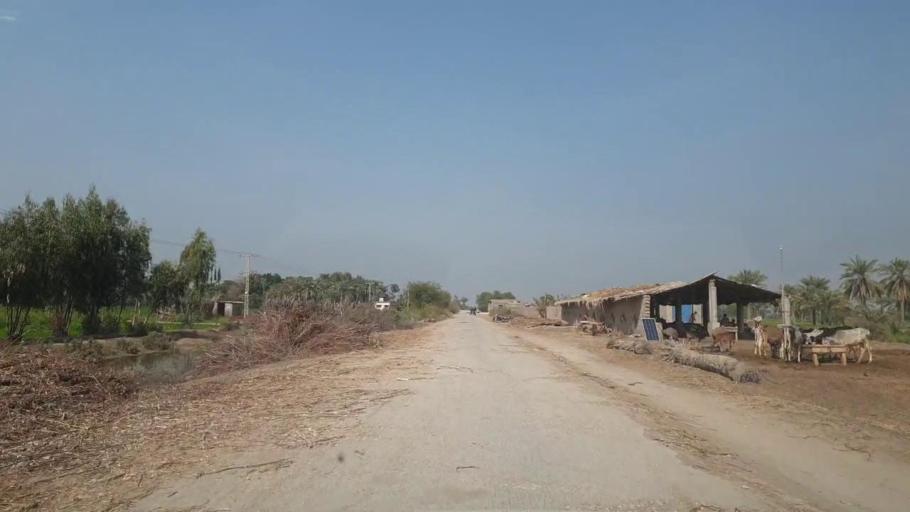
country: PK
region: Sindh
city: Mirpur Khas
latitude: 25.6843
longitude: 69.1552
